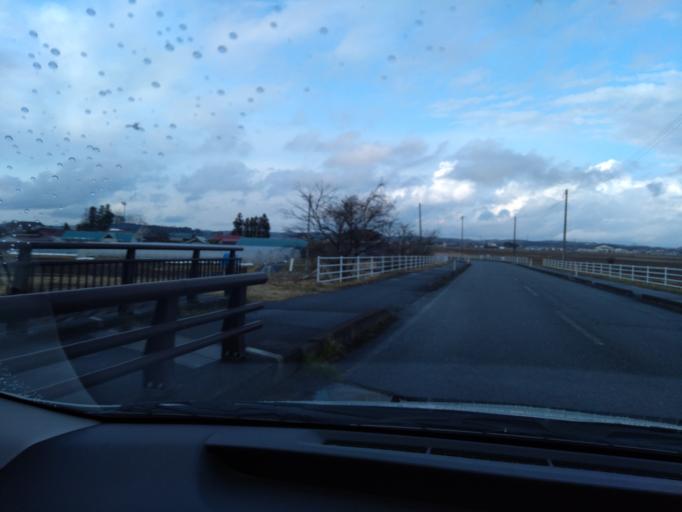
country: JP
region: Iwate
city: Ichinoseki
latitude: 38.7543
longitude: 141.1168
